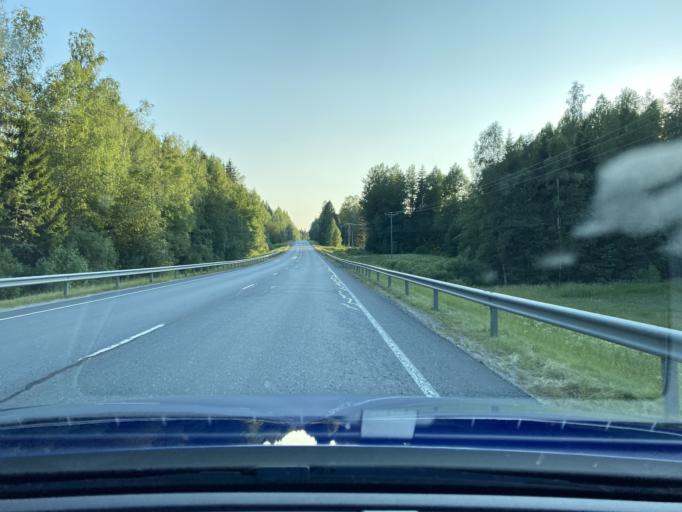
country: FI
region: Haeme
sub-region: Forssa
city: Tammela
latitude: 60.8271
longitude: 23.9225
